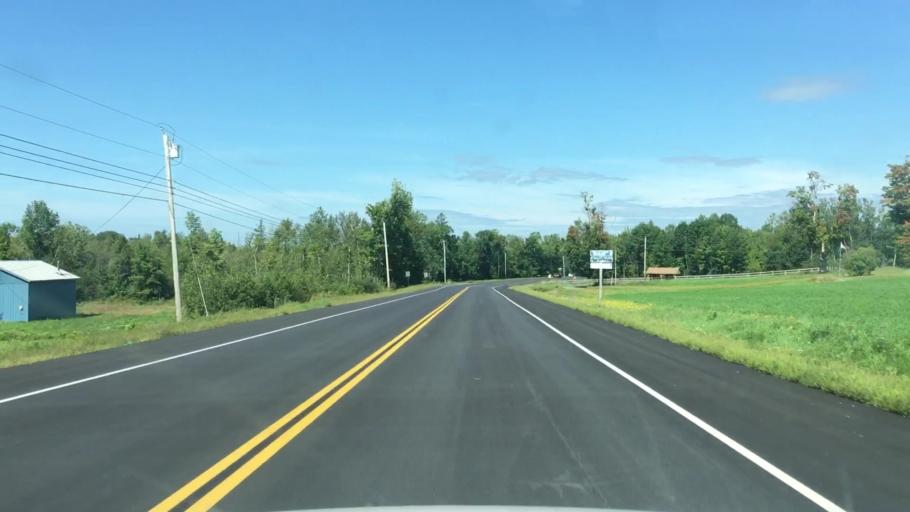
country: US
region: Maine
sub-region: Penobscot County
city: Corinna
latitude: 44.9551
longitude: -69.2605
